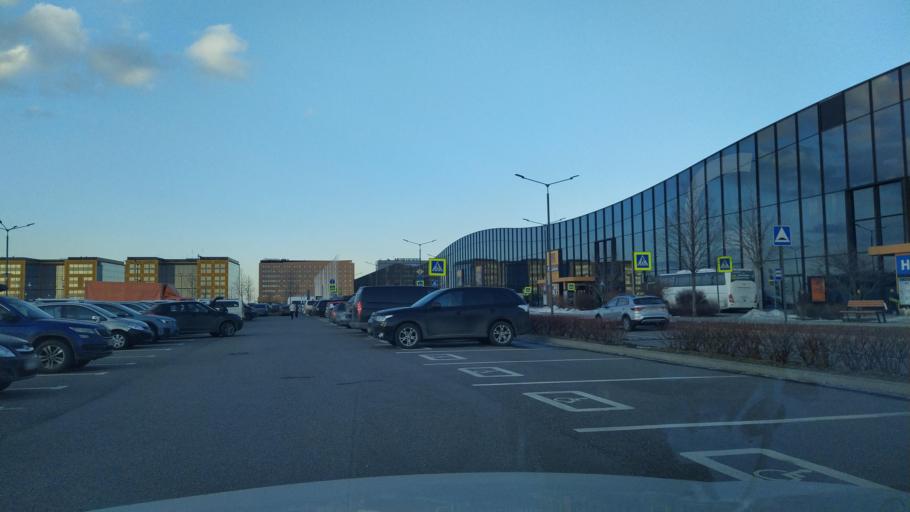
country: RU
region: St.-Petersburg
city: Aleksandrovskaya
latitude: 59.7599
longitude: 30.3513
